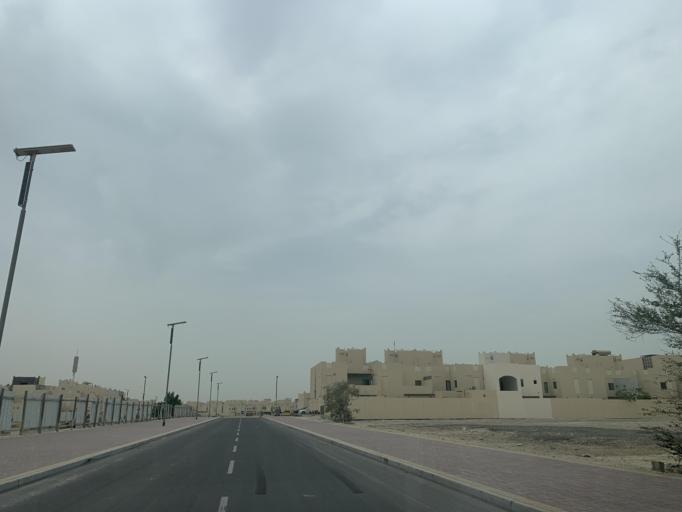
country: BH
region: Northern
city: Madinat `Isa
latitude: 26.1693
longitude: 50.5152
